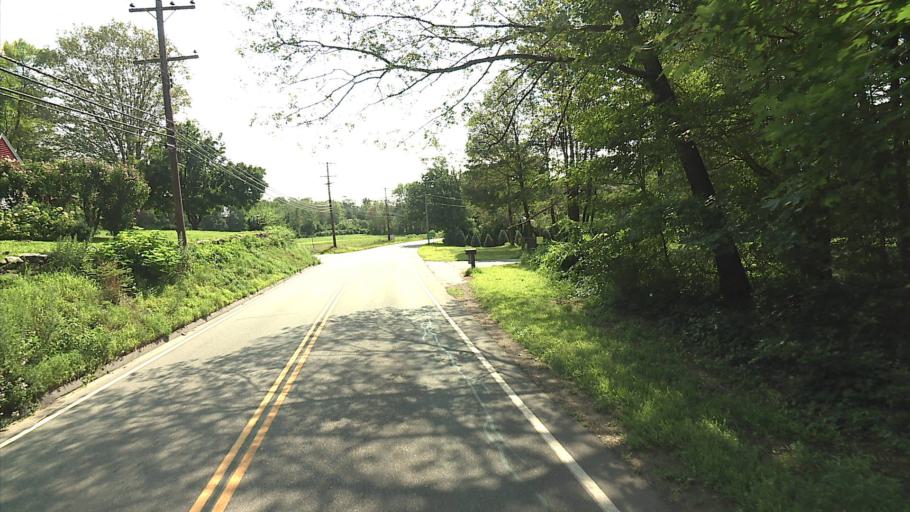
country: US
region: Connecticut
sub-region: New London County
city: Montville Center
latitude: 41.5648
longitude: -72.1622
